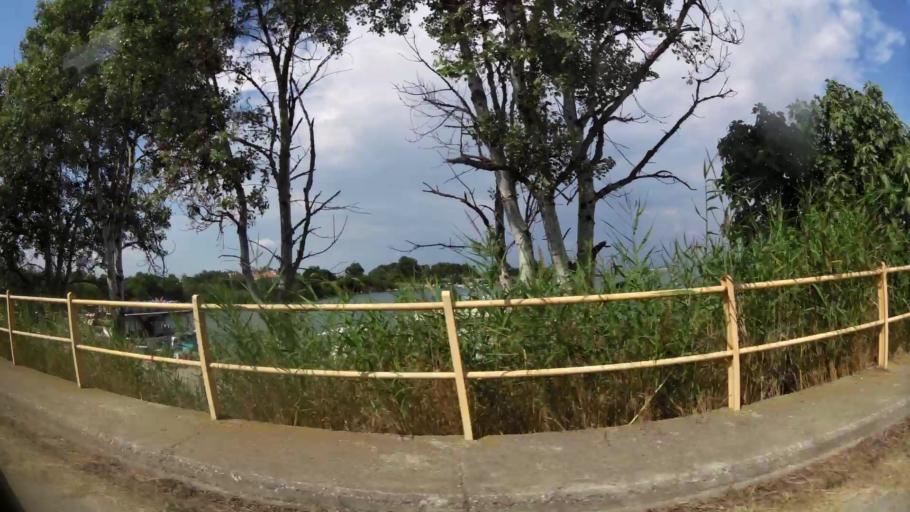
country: GR
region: Central Macedonia
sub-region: Nomos Pierias
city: Makrygialos
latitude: 40.3766
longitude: 22.6240
